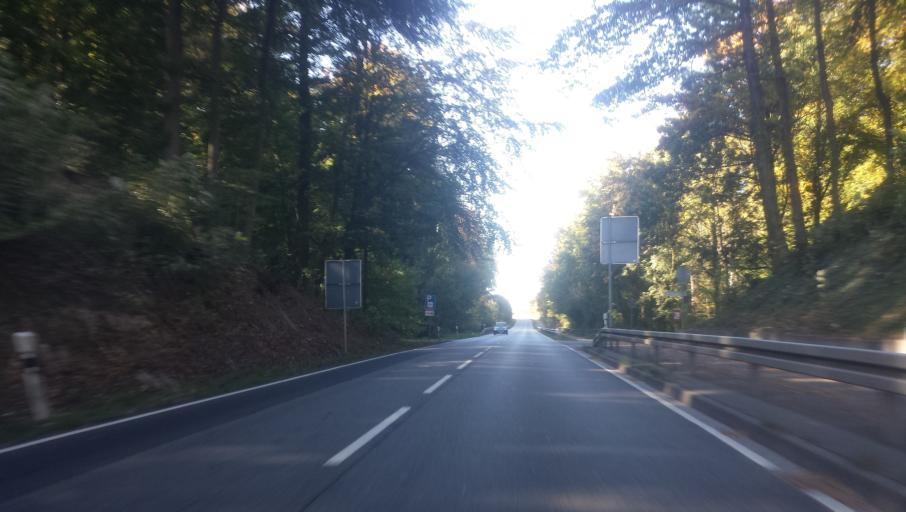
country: DE
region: Hesse
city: Ober-Ramstadt
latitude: 49.8168
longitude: 8.7702
